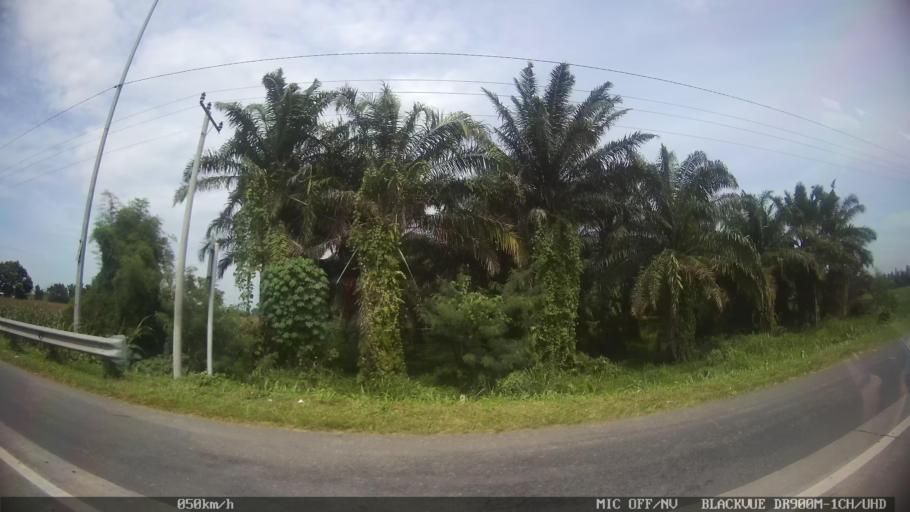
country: ID
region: North Sumatra
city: Sunggal
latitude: 3.6232
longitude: 98.6279
